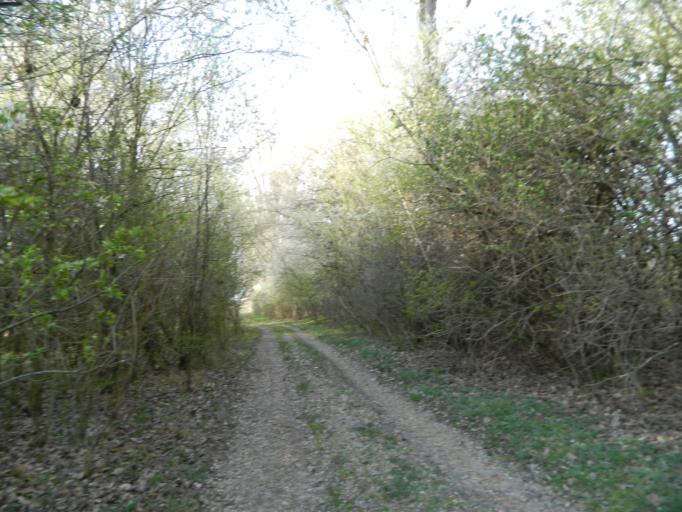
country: HU
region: Fejer
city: Pakozd
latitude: 47.2180
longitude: 18.4923
